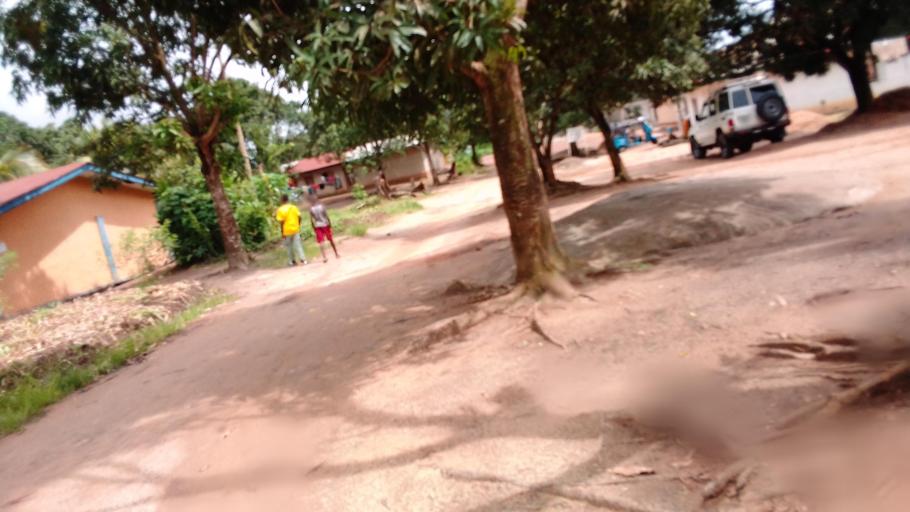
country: SL
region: Eastern Province
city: Kenema
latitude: 7.8651
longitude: -11.1779
